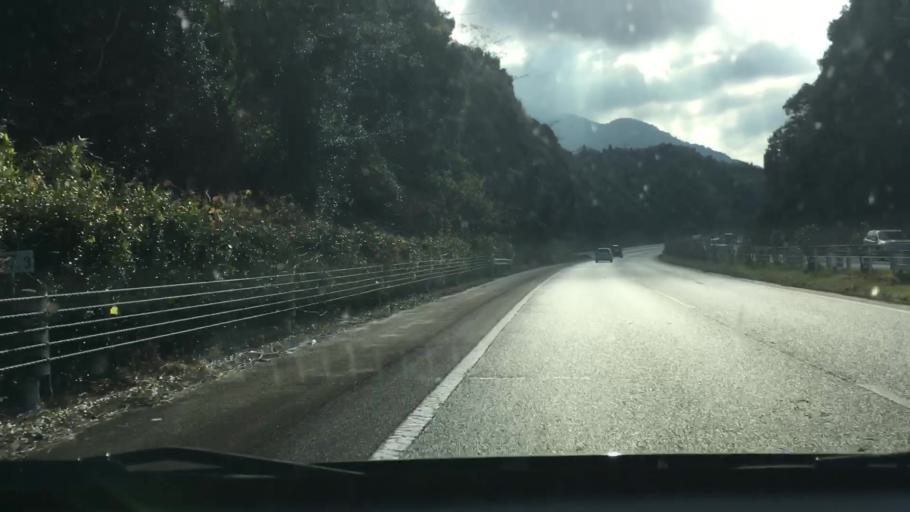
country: JP
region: Kumamoto
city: Matsubase
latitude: 32.5522
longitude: 130.6938
